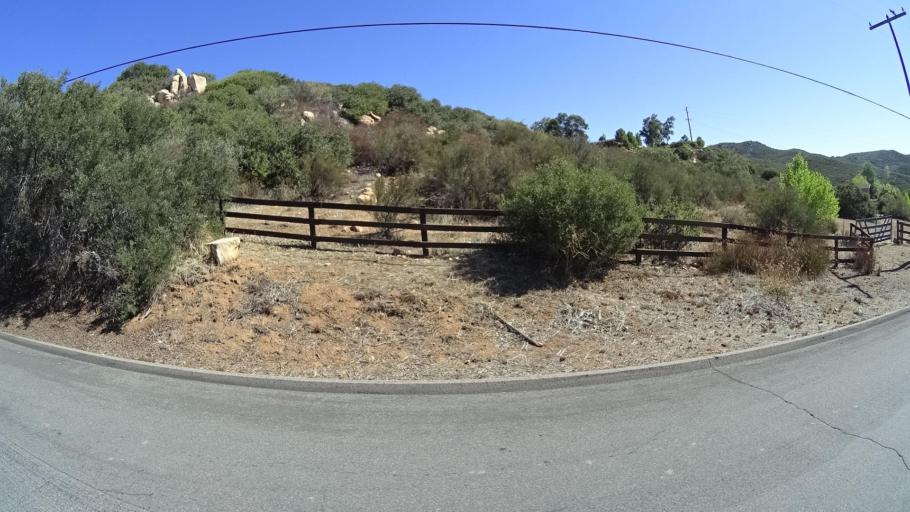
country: US
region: California
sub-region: San Diego County
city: Descanso
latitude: 32.8079
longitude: -116.6402
